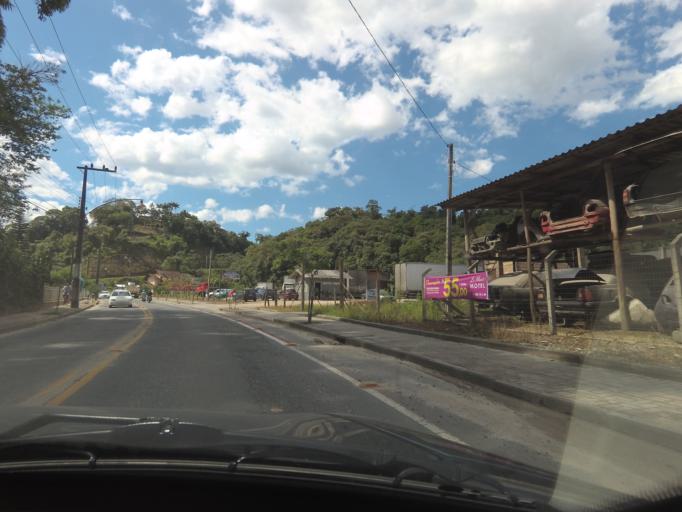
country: BR
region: Santa Catarina
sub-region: Brusque
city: Brusque
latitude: -27.0774
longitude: -48.9174
